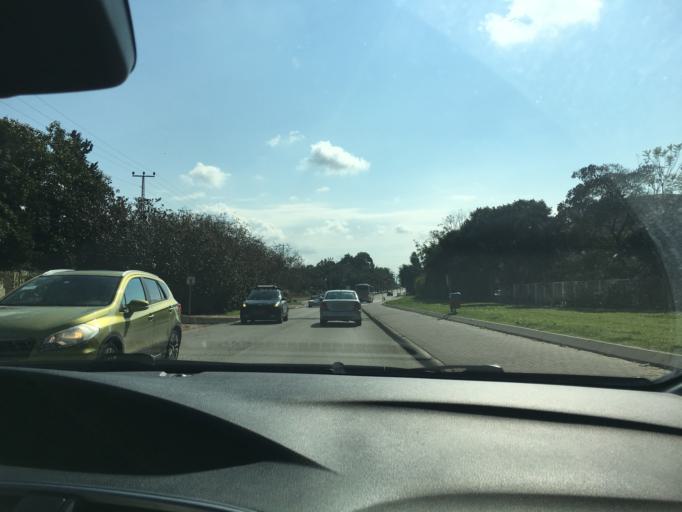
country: IL
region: Tel Aviv
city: Ramat HaSharon
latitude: 32.1643
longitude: 34.8530
